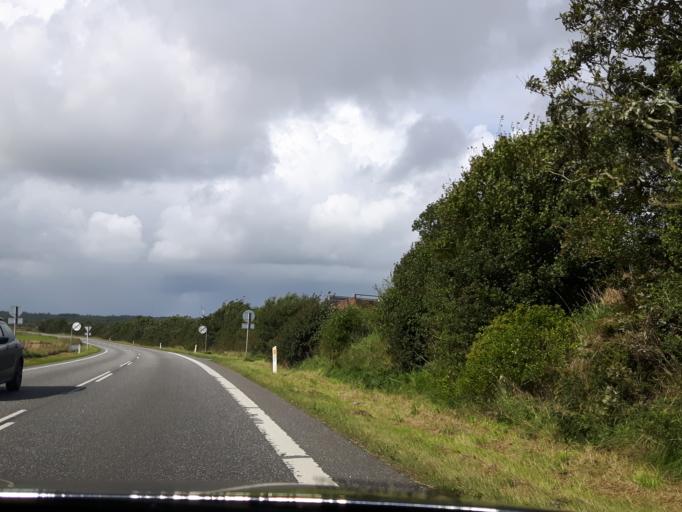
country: DK
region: North Denmark
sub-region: Morso Kommune
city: Nykobing Mors
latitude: 57.0361
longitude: 8.9673
